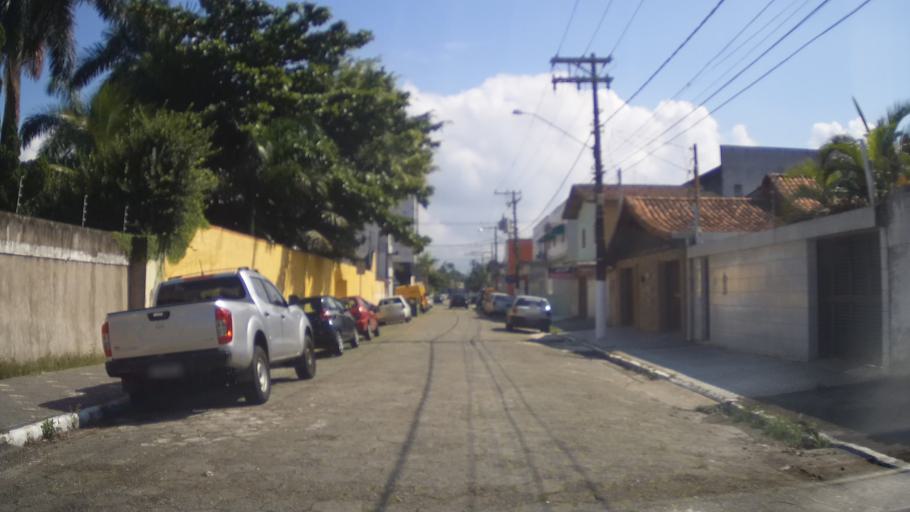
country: BR
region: Sao Paulo
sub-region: Praia Grande
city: Praia Grande
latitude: -24.0049
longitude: -46.4203
